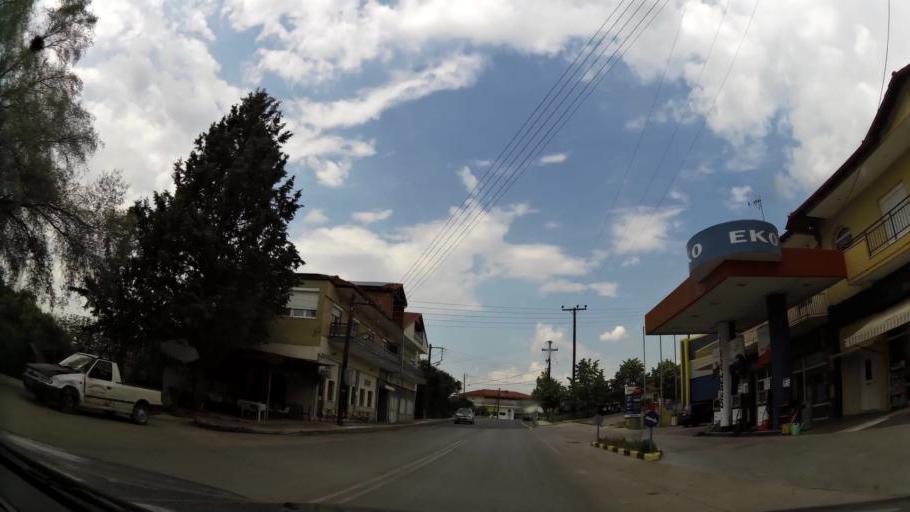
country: GR
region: West Macedonia
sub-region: Nomos Kozanis
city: Koila
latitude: 40.3492
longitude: 21.8288
